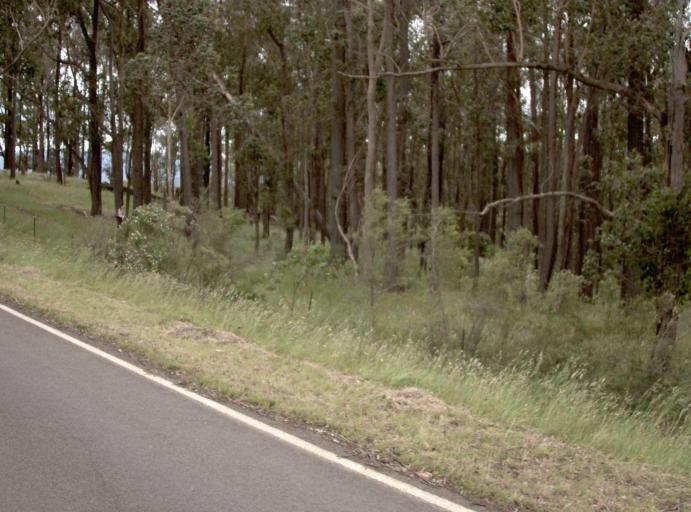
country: AU
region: Victoria
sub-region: Latrobe
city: Moe
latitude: -38.0204
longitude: 146.1594
